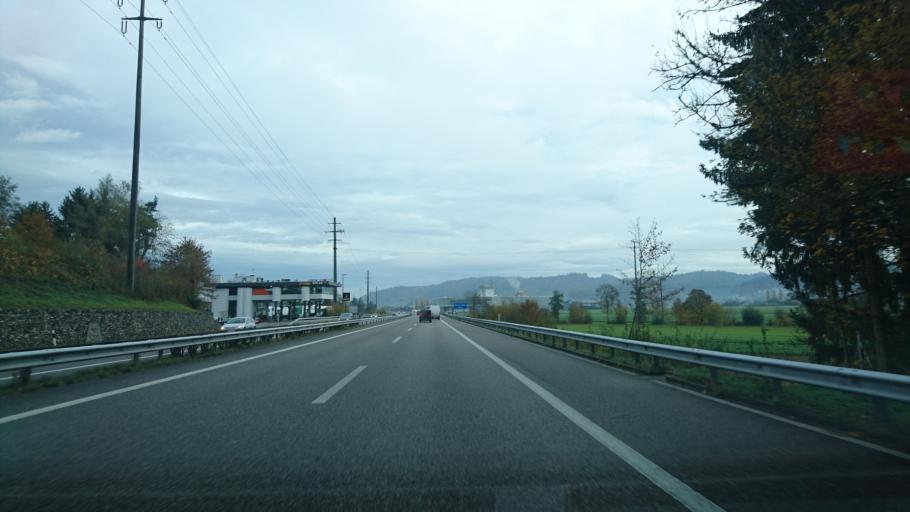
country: CH
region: Aargau
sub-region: Bezirk Zofingen
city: Kolliken
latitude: 47.3287
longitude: 8.0292
